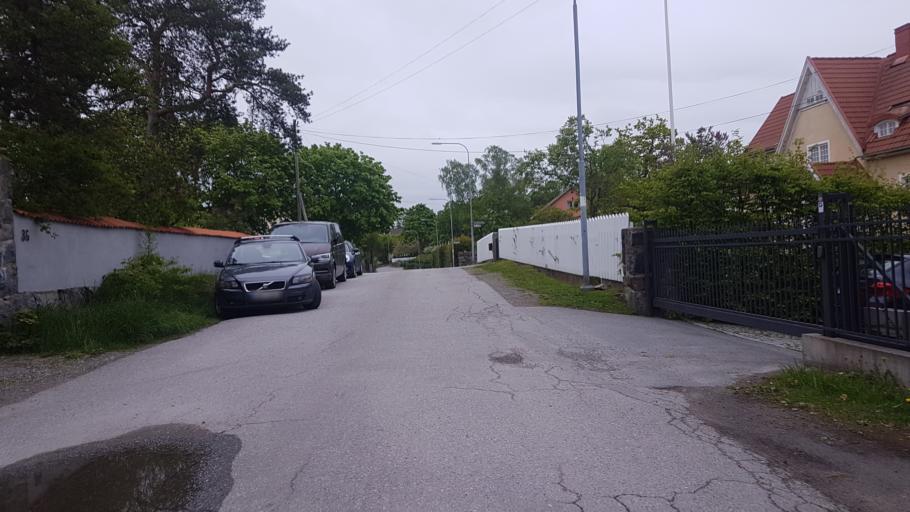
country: SE
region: Stockholm
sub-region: Lidingo
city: Lidingoe
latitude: 59.3596
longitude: 18.1265
